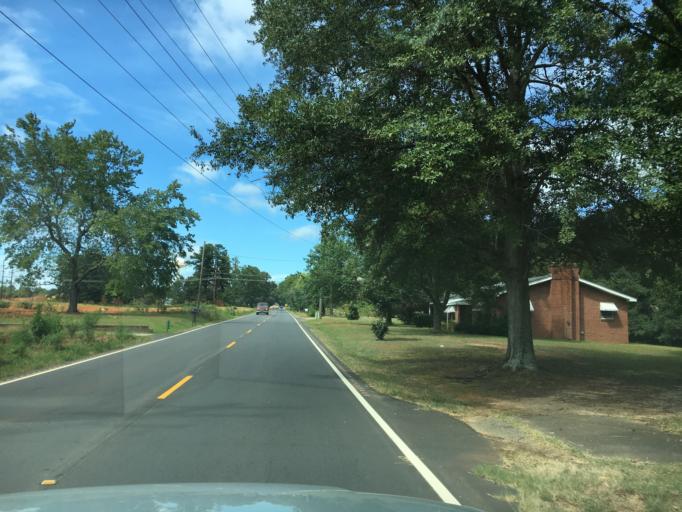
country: US
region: South Carolina
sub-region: Spartanburg County
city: Duncan
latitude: 34.9504
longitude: -82.1430
